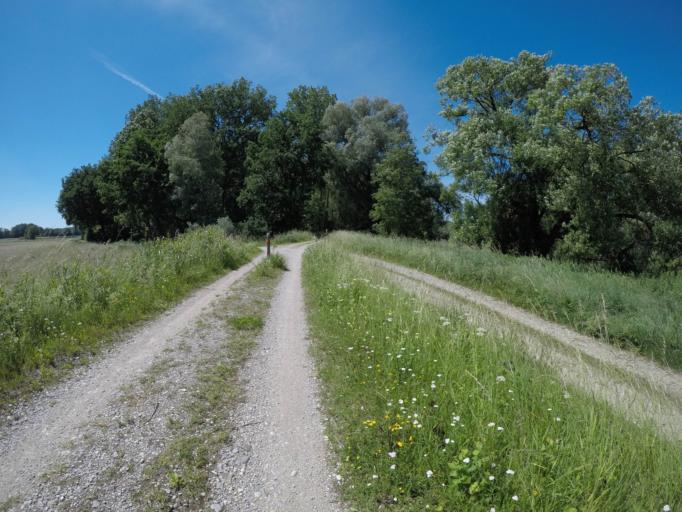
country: DE
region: Bavaria
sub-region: Upper Bavaria
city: Langenbach
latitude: 48.4605
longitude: 11.8830
